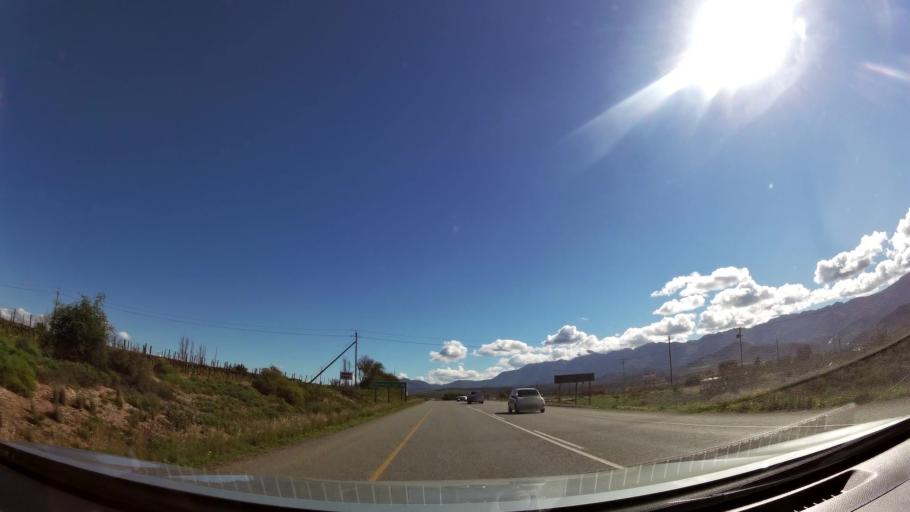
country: ZA
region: Western Cape
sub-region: Cape Winelands District Municipality
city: Ashton
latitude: -33.8288
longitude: 19.9896
